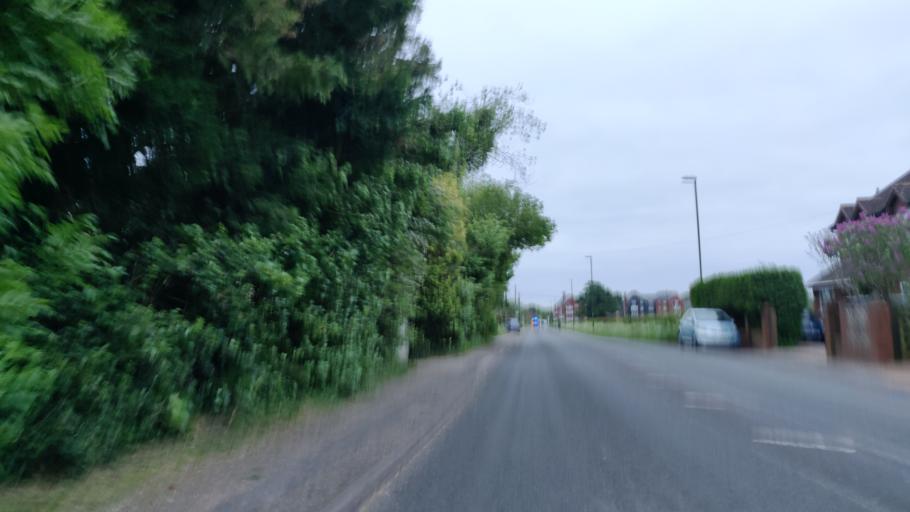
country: GB
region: England
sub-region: West Sussex
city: Southwater
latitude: 51.0327
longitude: -0.3514
